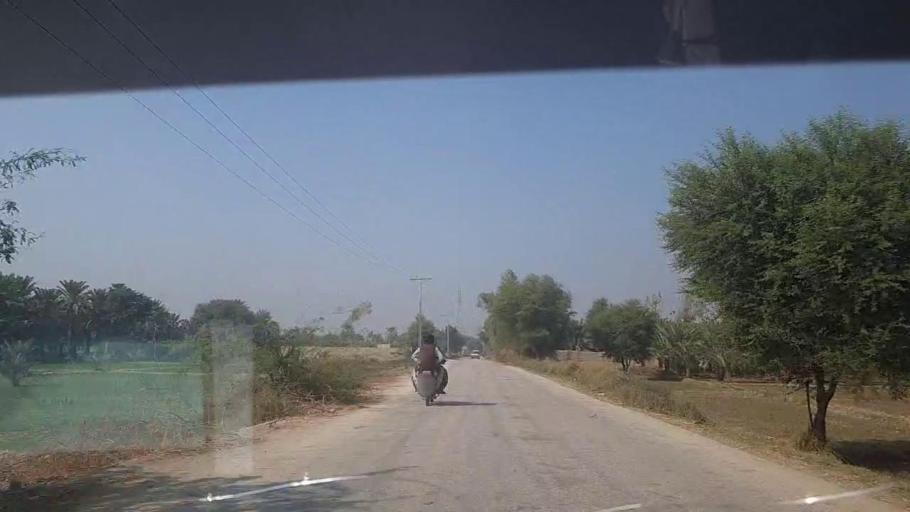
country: PK
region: Sindh
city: Kot Diji
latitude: 27.3636
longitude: 68.7054
